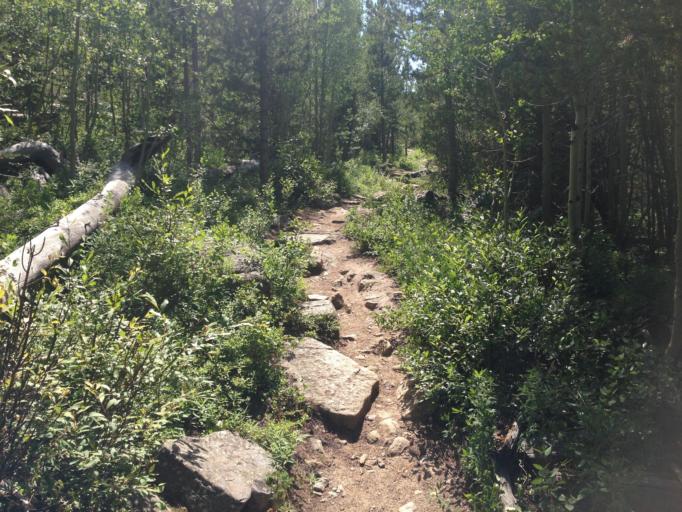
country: US
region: Colorado
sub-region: Larimer County
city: Estes Park
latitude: 40.1953
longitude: -105.5723
